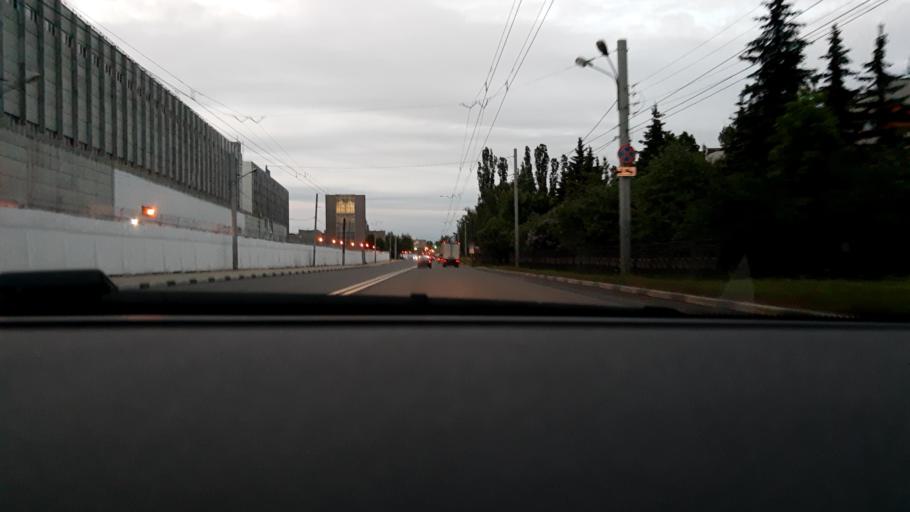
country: RU
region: Nizjnij Novgorod
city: Nizhniy Novgorod
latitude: 56.3167
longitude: 43.9023
